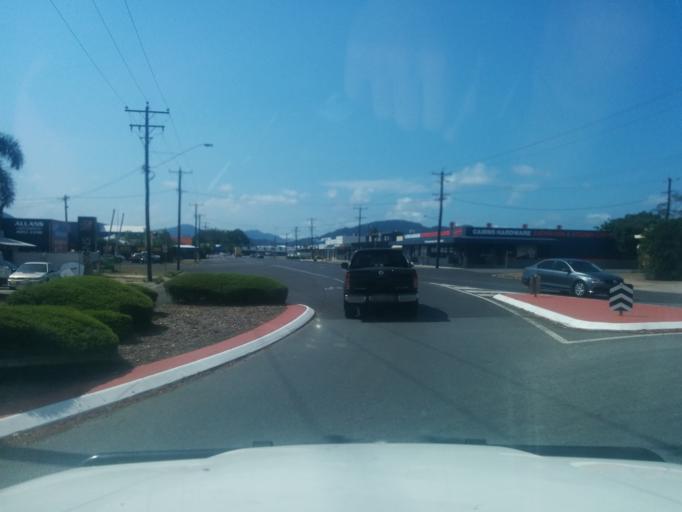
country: AU
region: Queensland
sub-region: Cairns
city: Woree
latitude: -16.9382
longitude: 145.7547
